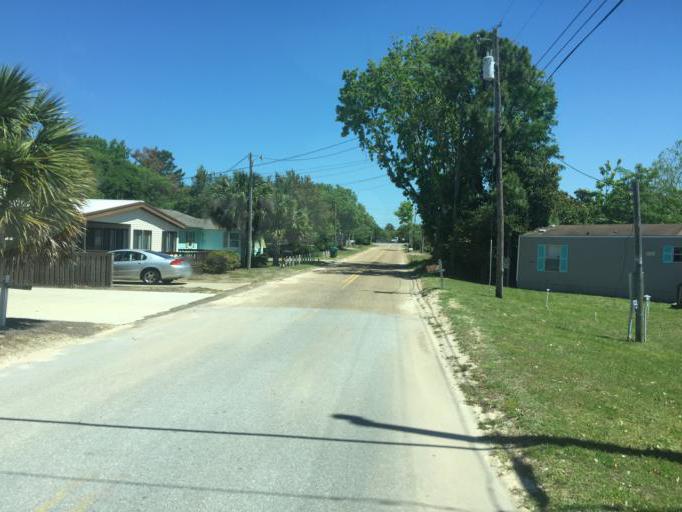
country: US
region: Florida
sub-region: Bay County
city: Laguna Beach
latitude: 30.2438
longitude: -85.9244
